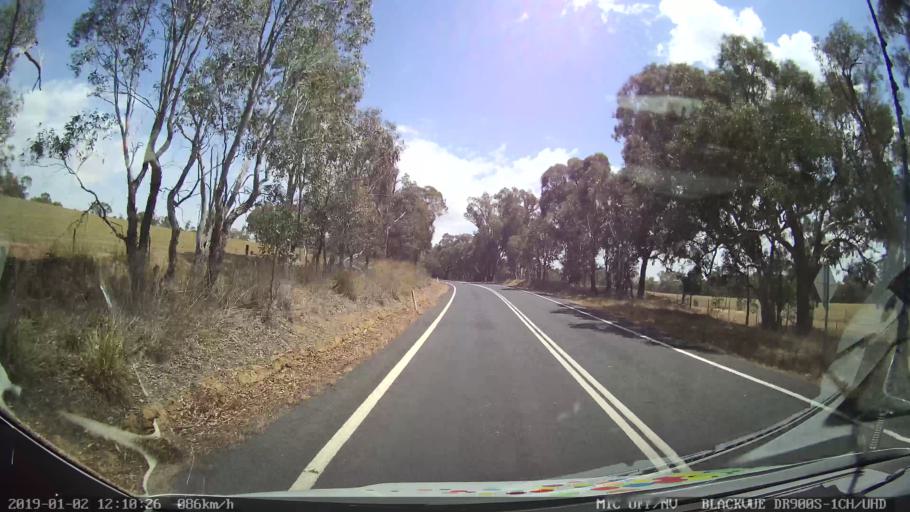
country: AU
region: New South Wales
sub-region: Young
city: Young
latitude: -34.4603
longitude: 148.2636
